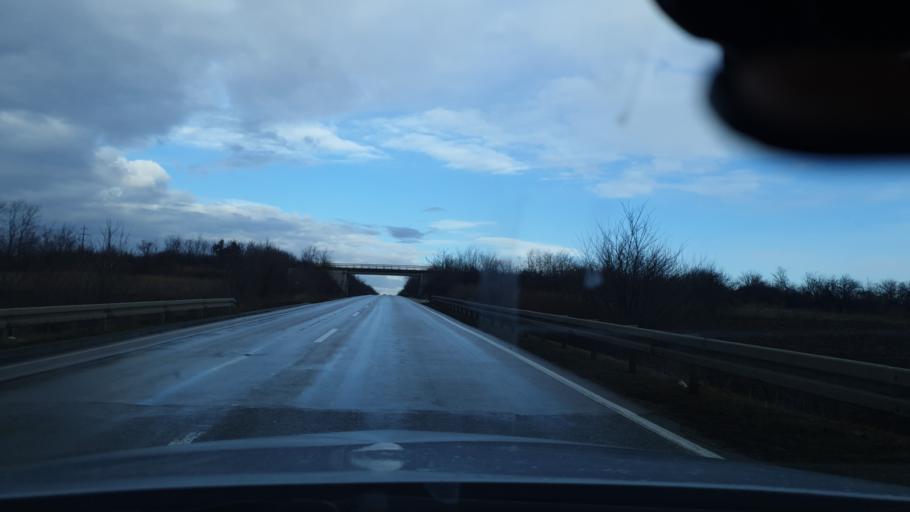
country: RS
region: Central Serbia
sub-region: Podunavski Okrug
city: Smederevo
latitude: 44.5960
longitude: 20.9563
